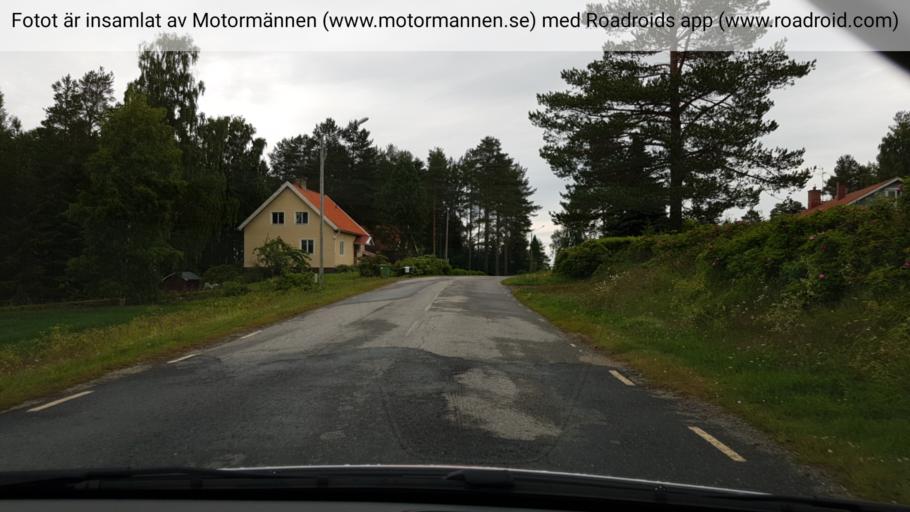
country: SE
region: Vaesterbotten
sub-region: Vannas Kommun
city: Vannasby
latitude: 64.0861
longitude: 19.9495
